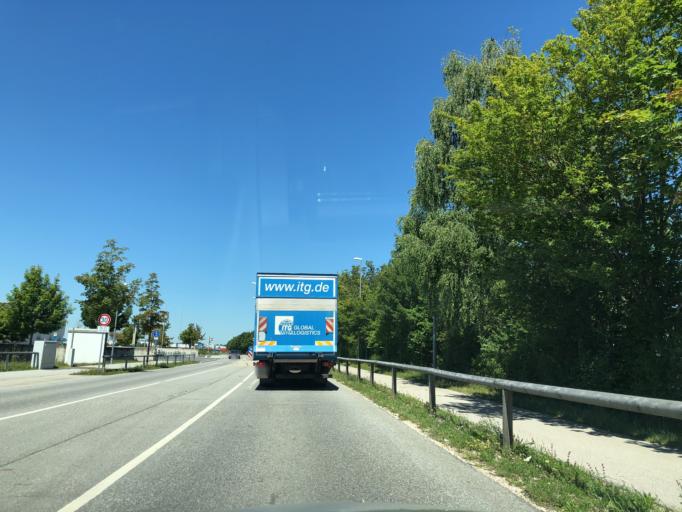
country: DE
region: Bavaria
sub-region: Upper Bavaria
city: Erding
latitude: 48.2969
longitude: 11.8919
